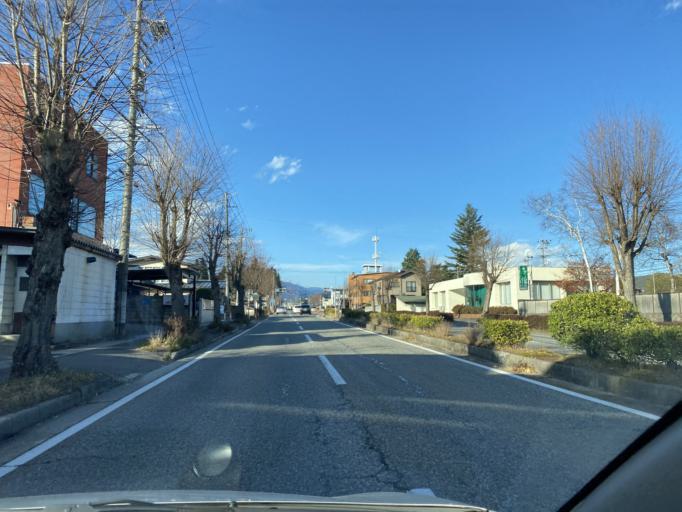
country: JP
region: Nagano
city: Omachi
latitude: 36.5041
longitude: 137.8550
